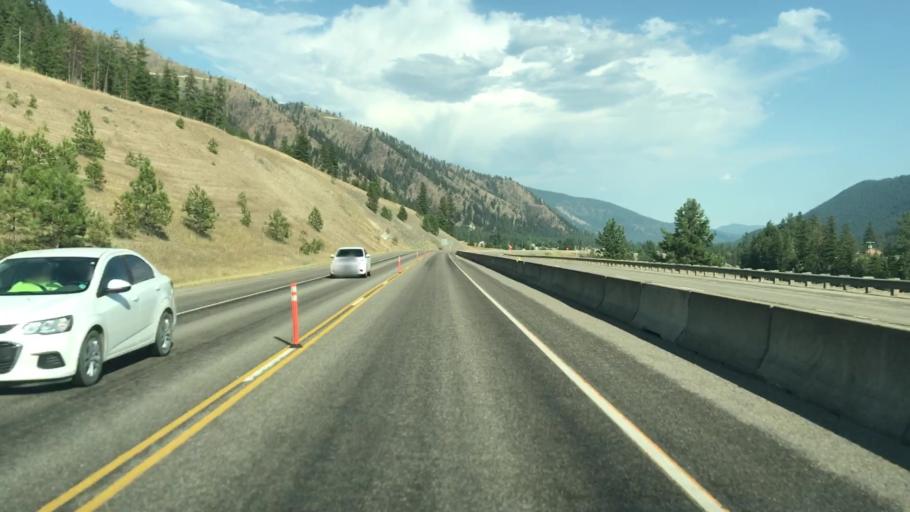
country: US
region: Montana
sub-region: Mineral County
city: Superior
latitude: 47.2170
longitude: -114.9527
